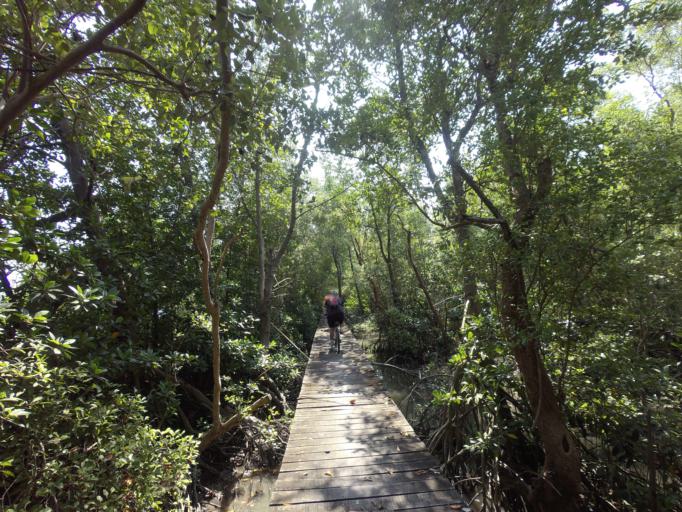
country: TH
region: Bangkok
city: Thung Khru
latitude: 13.5075
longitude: 100.4234
